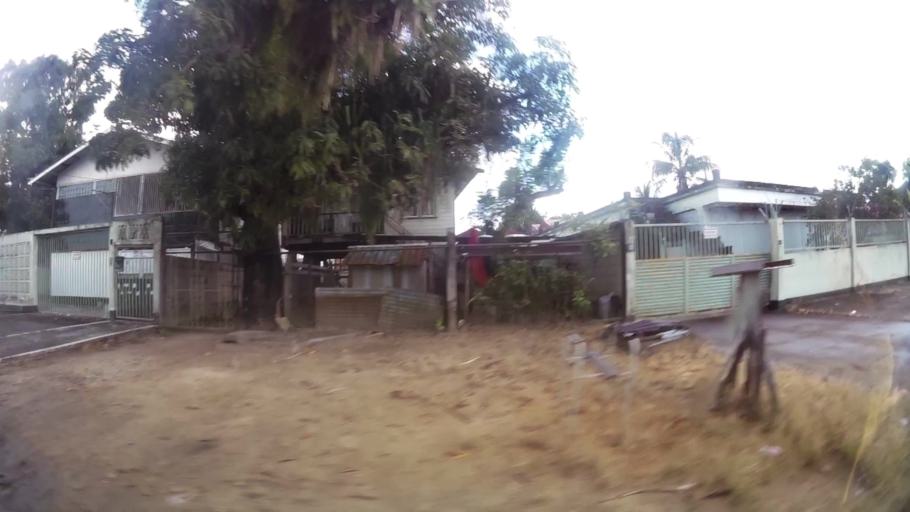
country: SR
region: Paramaribo
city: Paramaribo
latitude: 5.8324
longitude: -55.1461
